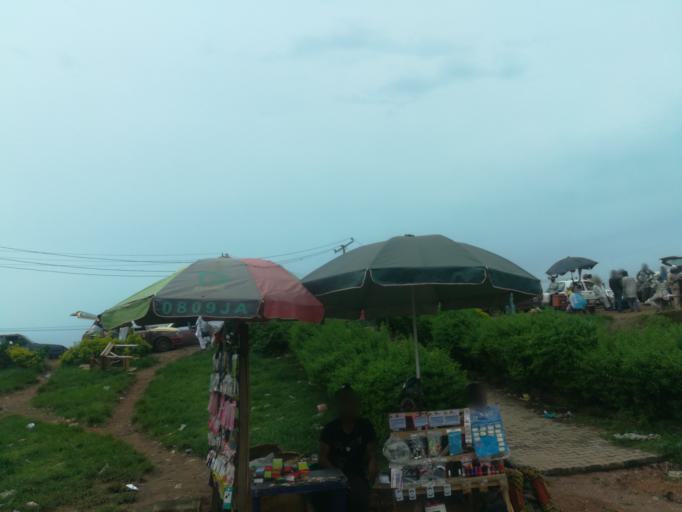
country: NG
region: Oyo
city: Ibadan
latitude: 7.4017
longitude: 3.9436
